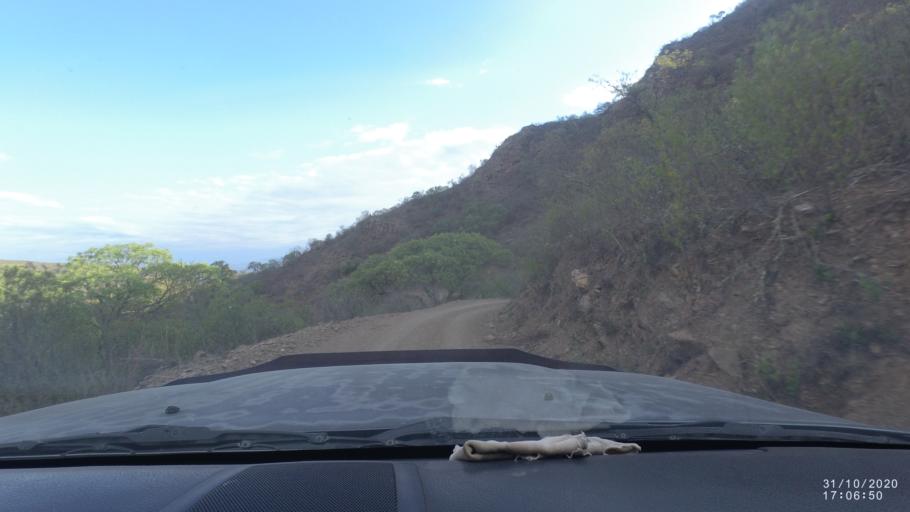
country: BO
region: Chuquisaca
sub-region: Provincia Zudanez
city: Mojocoya
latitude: -18.5444
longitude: -64.5434
